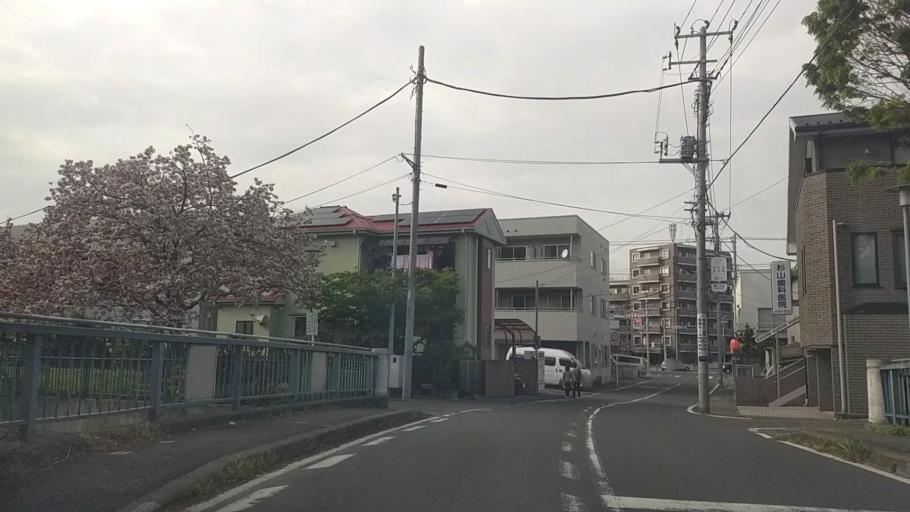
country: JP
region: Kanagawa
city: Kamakura
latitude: 35.3628
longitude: 139.5569
